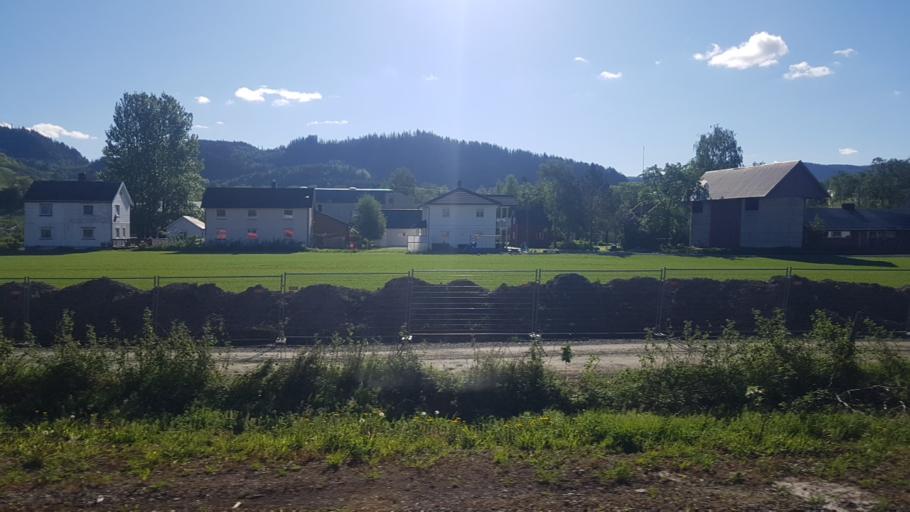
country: NO
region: Sor-Trondelag
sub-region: Melhus
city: Lundamo
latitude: 63.1986
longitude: 10.3049
